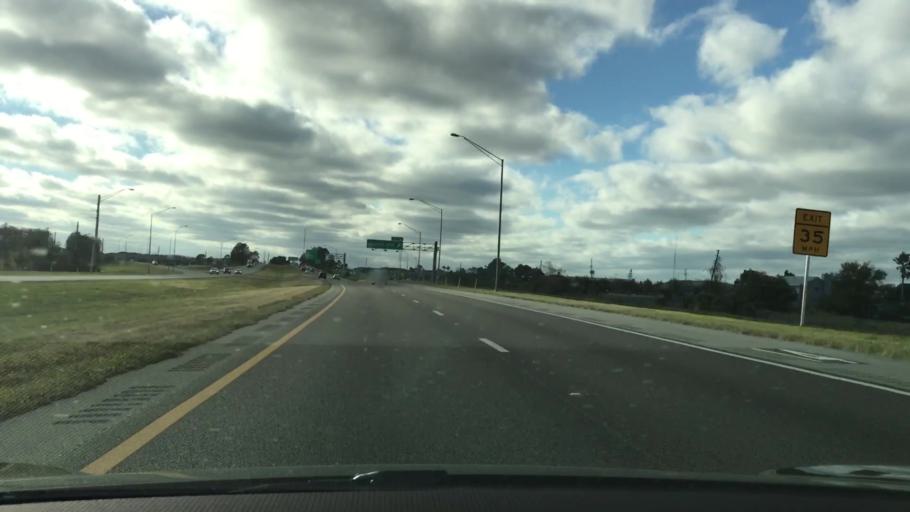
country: US
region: Florida
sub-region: Orange County
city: Meadow Woods
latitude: 28.3700
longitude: -81.3589
